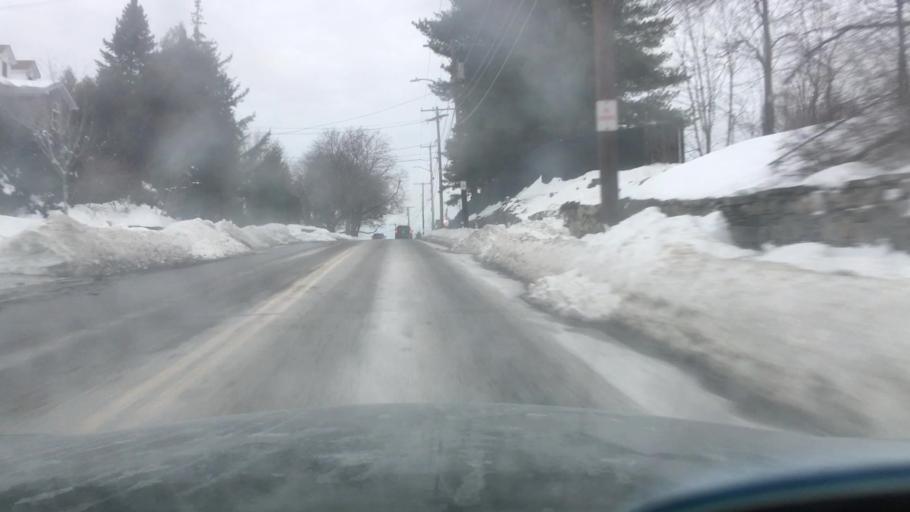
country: US
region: Massachusetts
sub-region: Middlesex County
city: Watertown
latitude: 42.3767
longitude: -71.1767
